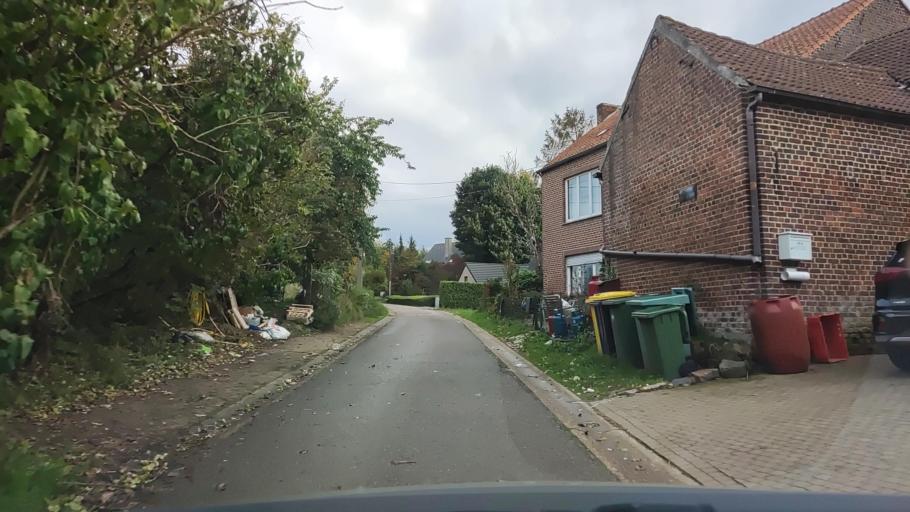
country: BE
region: Wallonia
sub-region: Province du Brabant Wallon
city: Jodoigne
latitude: 50.7038
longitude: 4.8810
